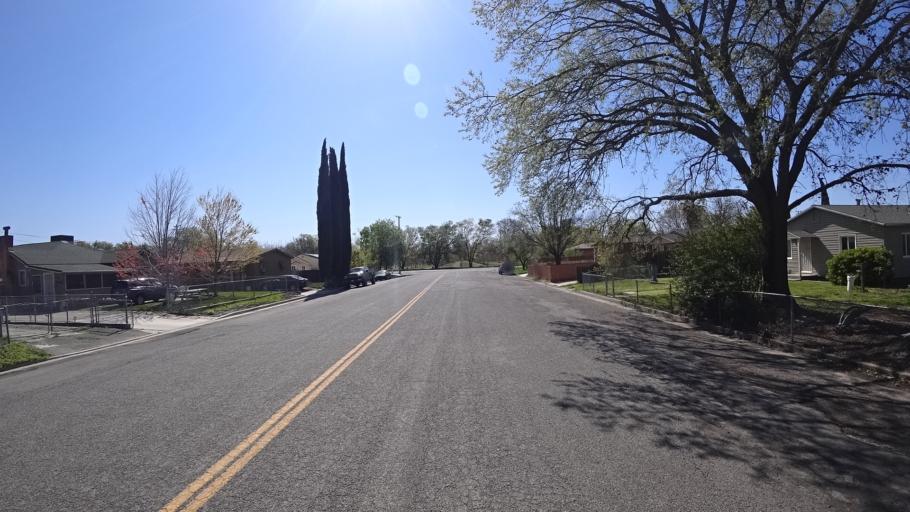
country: US
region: California
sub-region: Glenn County
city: Hamilton City
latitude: 39.7382
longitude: -122.0149
